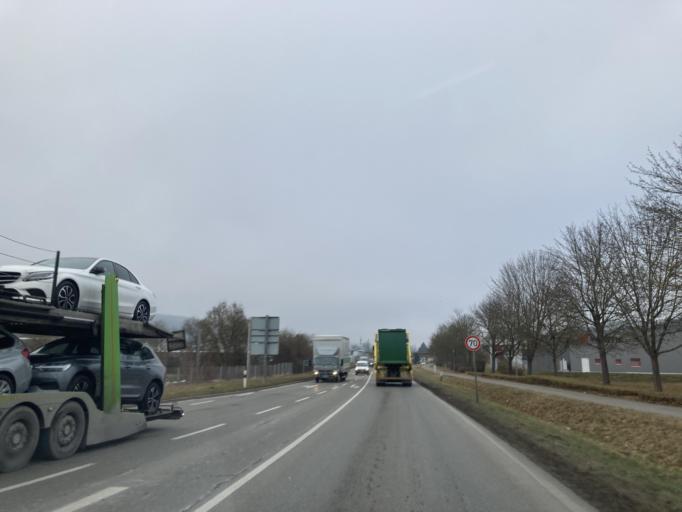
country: DE
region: Baden-Wuerttemberg
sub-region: Freiburg Region
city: Wurmlingen
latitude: 47.9619
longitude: 8.7826
